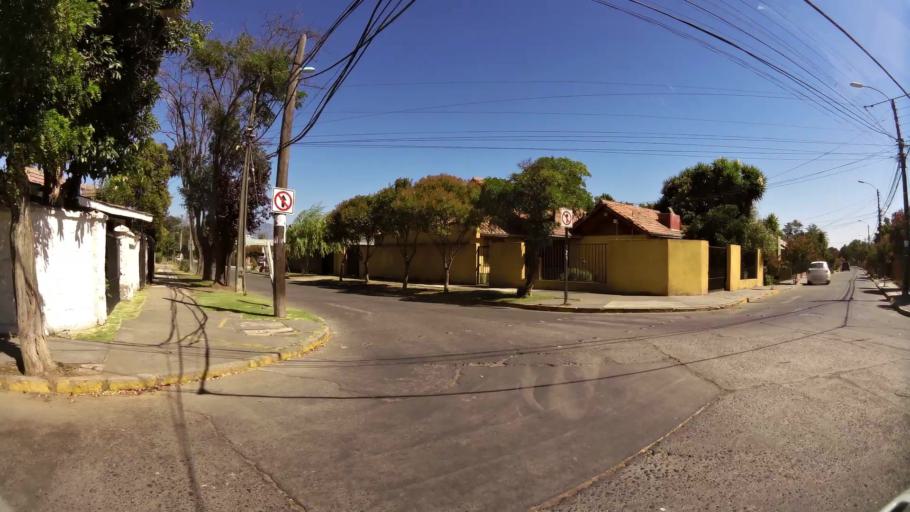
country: CL
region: O'Higgins
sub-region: Provincia de Cachapoal
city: Rancagua
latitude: -34.1741
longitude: -70.7308
